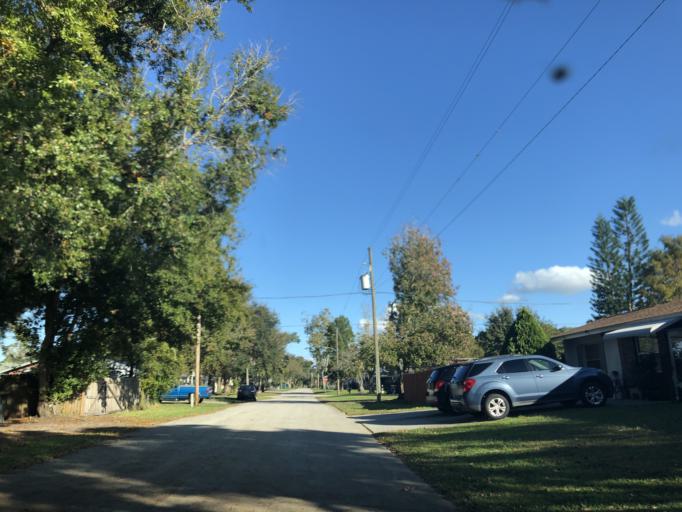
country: US
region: Florida
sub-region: Osceola County
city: Saint Cloud
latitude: 28.2516
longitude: -81.3002
